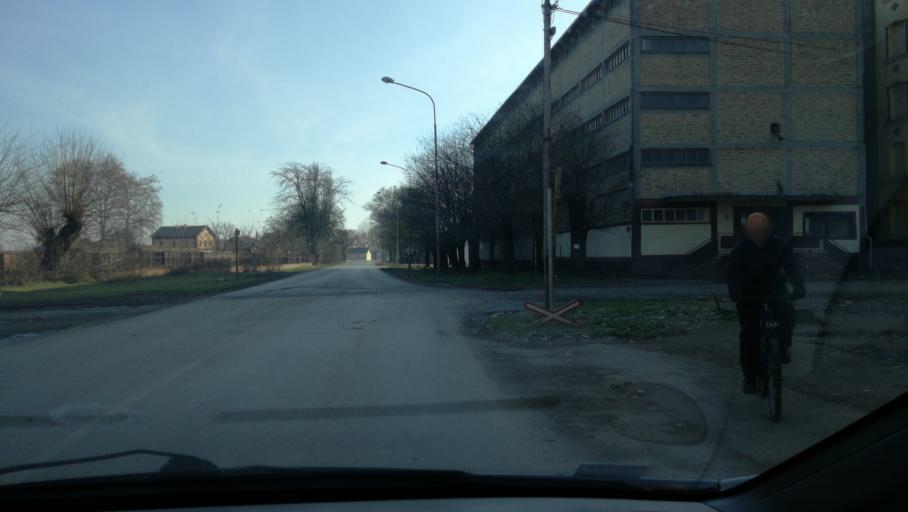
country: RS
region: Autonomna Pokrajina Vojvodina
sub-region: Severnobanatski Okrug
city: Kikinda
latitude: 45.8396
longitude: 20.4858
